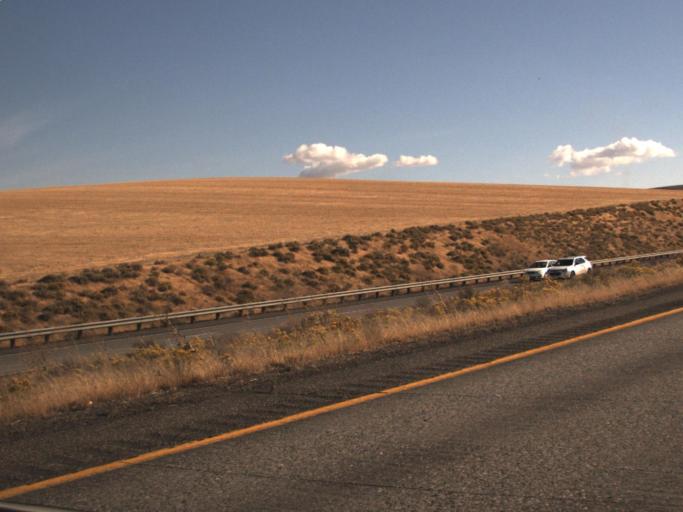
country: US
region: Washington
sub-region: Benton County
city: Highland
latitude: 46.1303
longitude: -119.2024
